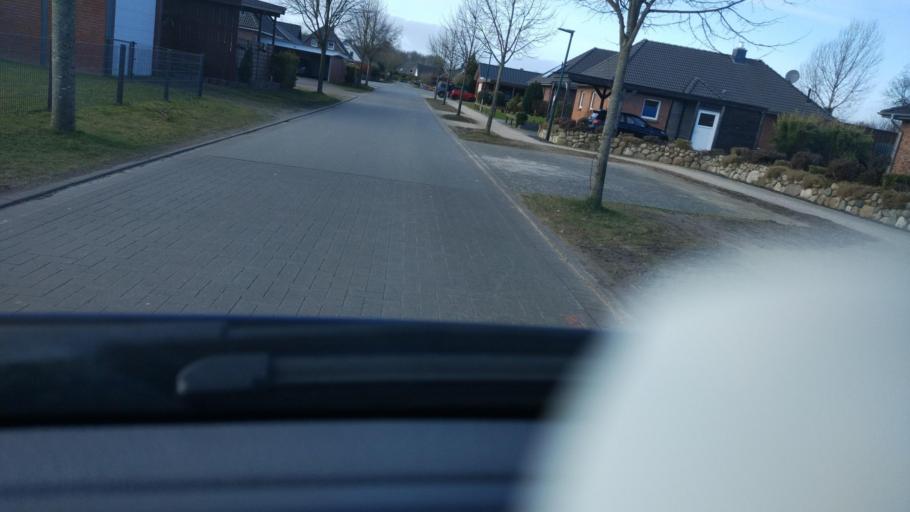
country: DE
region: Schleswig-Holstein
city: Silberstedt
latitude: 54.5180
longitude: 9.3634
